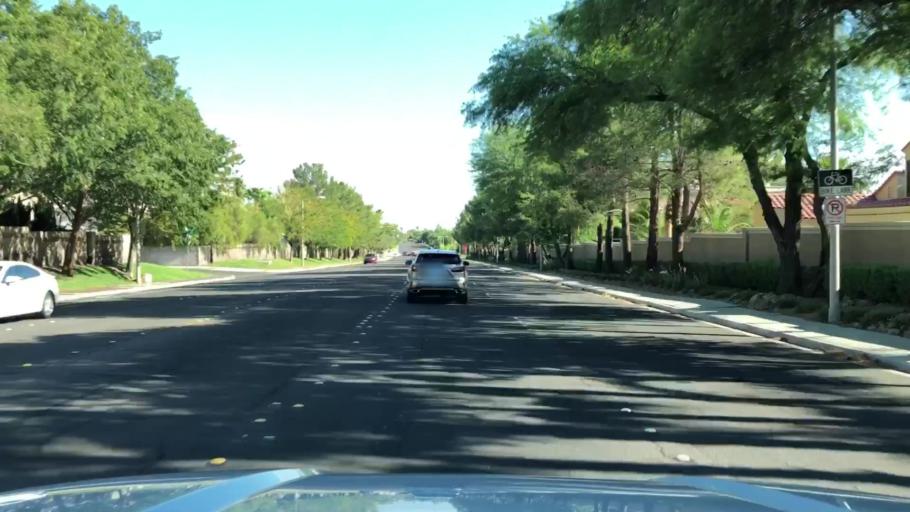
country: US
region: Nevada
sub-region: Clark County
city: Whitney
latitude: 36.0391
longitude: -115.0687
